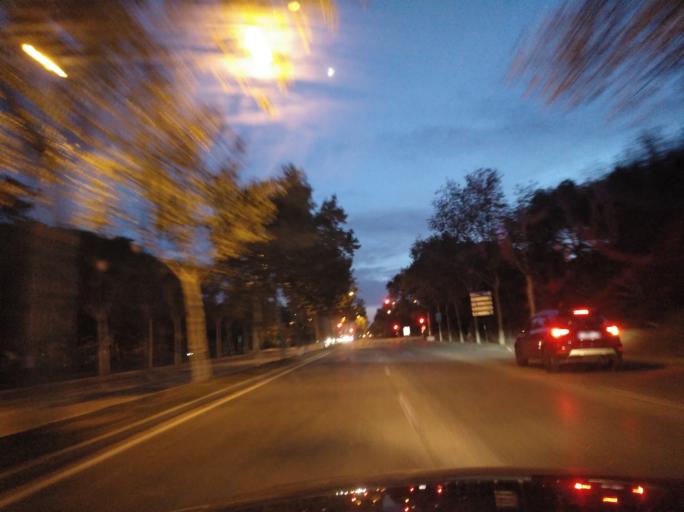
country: ES
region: Andalusia
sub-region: Provincia de Sevilla
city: Camas
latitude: 37.4049
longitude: -6.0102
